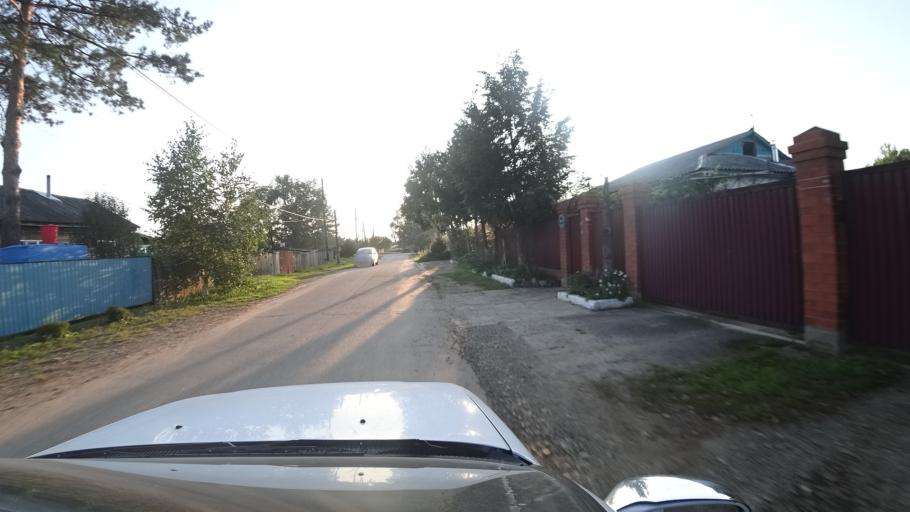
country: RU
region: Primorskiy
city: Dal'nerechensk
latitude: 45.9441
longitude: 133.7568
